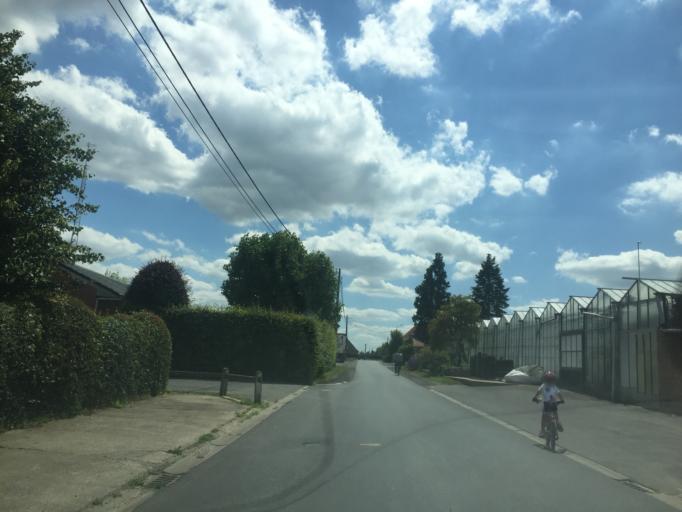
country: BE
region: Flanders
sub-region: Provincie West-Vlaanderen
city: Staden
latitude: 50.9556
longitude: 3.0124
